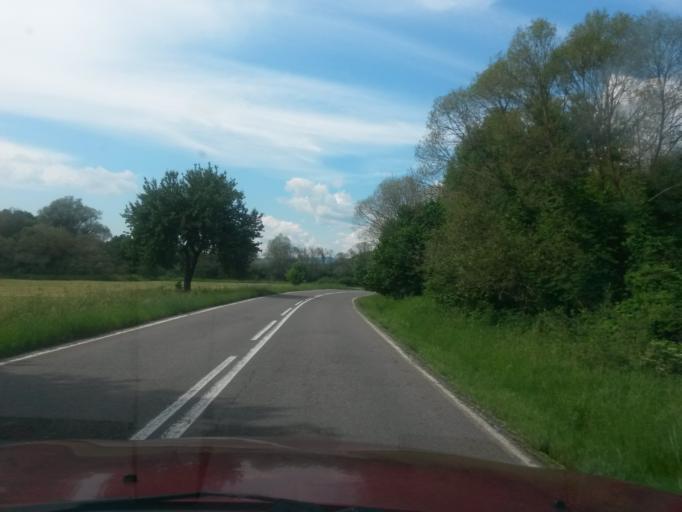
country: UA
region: Zakarpattia
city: Velykyi Bereznyi
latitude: 48.9116
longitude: 22.3722
